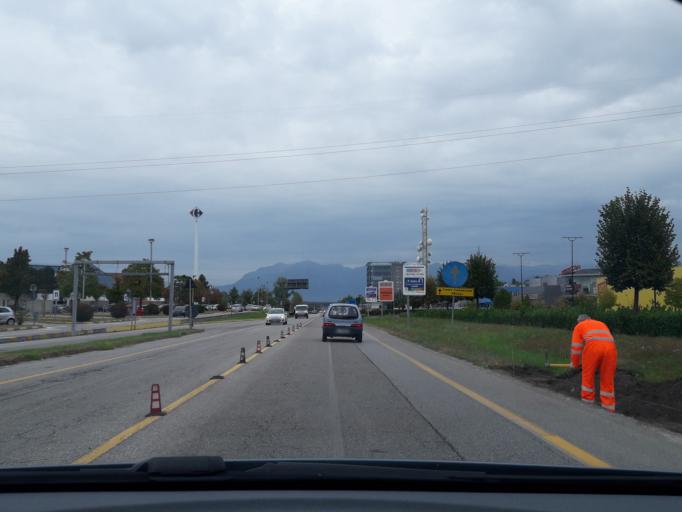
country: IT
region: Friuli Venezia Giulia
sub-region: Provincia di Udine
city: Tavagnacco
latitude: 46.1179
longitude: 13.2265
